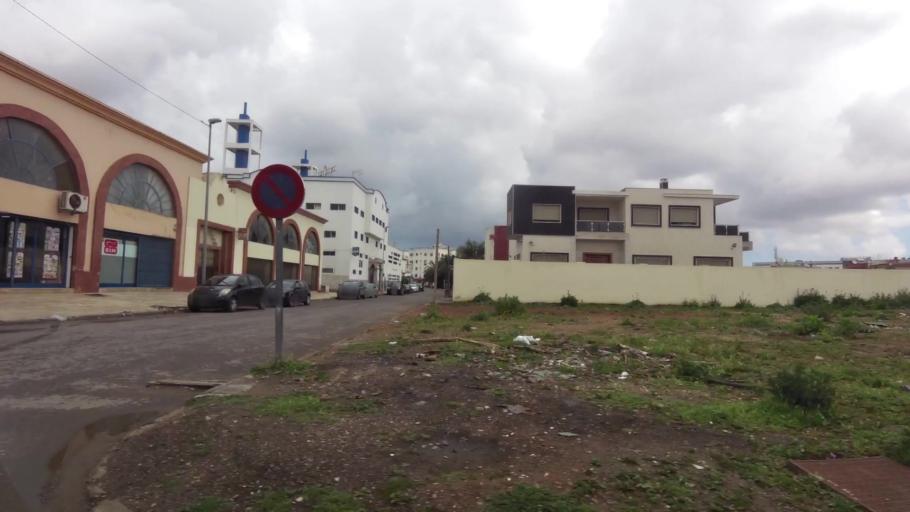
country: MA
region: Grand Casablanca
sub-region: Nouaceur
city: Bouskoura
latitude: 33.5188
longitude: -7.6442
